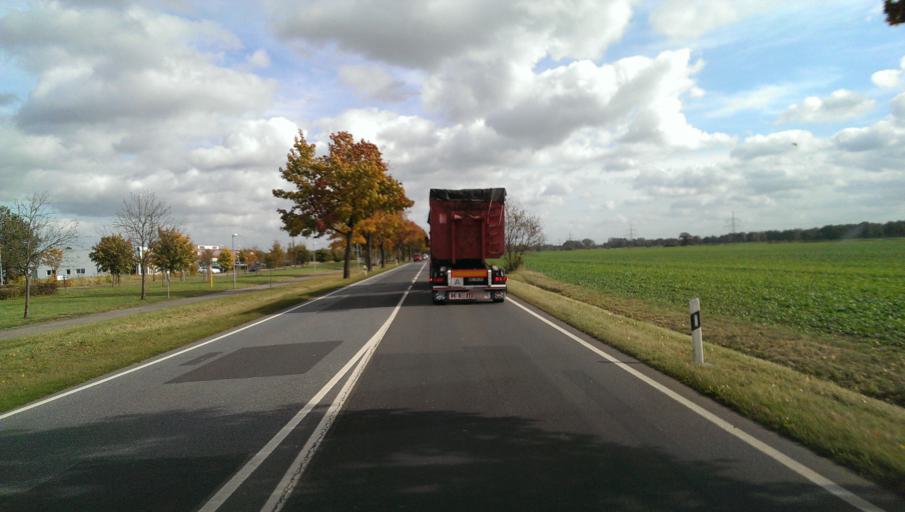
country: DE
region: Brandenburg
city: Schwarzheide
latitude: 51.4707
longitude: 13.8251
